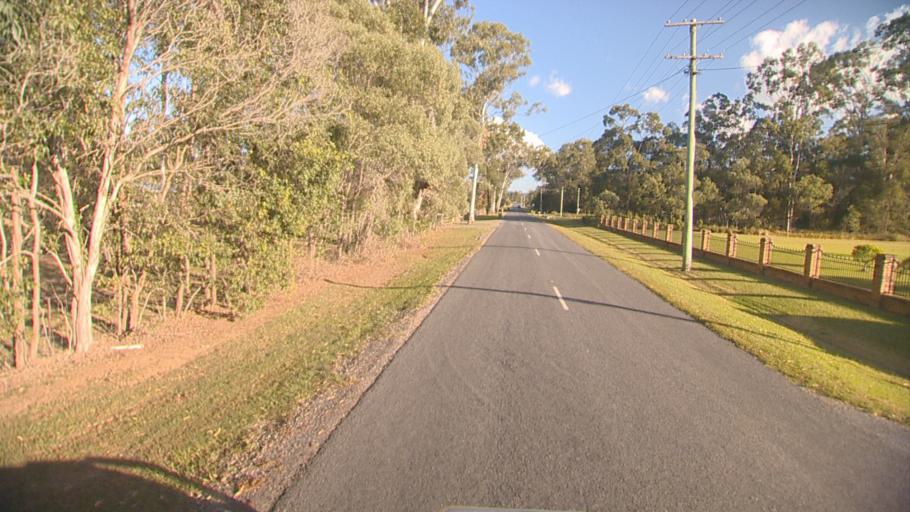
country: AU
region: Queensland
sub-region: Gold Coast
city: Yatala
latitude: -27.6724
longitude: 153.2437
